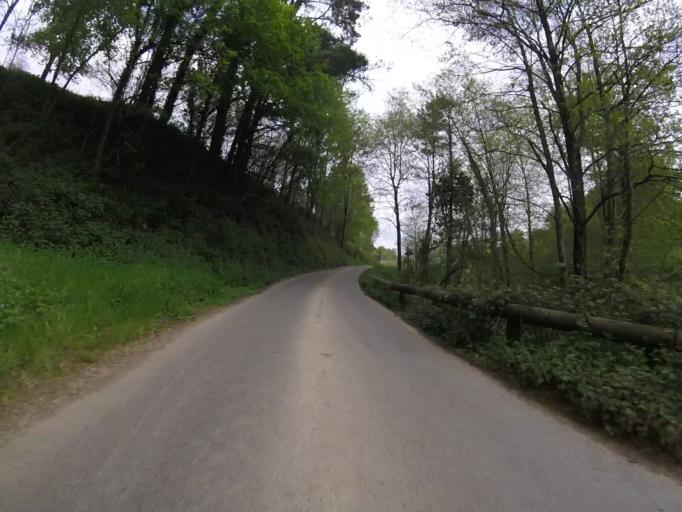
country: ES
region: Basque Country
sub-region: Provincia de Guipuzcoa
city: Zizurkil
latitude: 43.1830
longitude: -2.0829
